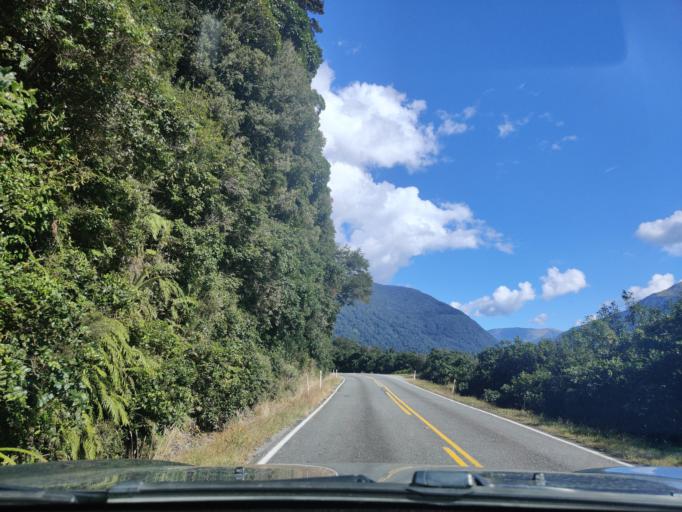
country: NZ
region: Otago
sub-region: Queenstown-Lakes District
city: Wanaka
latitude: -43.9706
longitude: 169.4143
